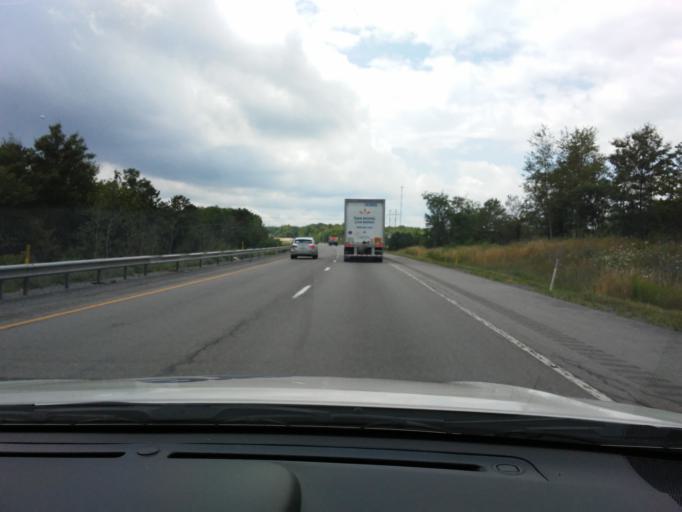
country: US
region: Pennsylvania
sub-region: Centre County
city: Milesburg
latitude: 41.0235
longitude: -77.9444
